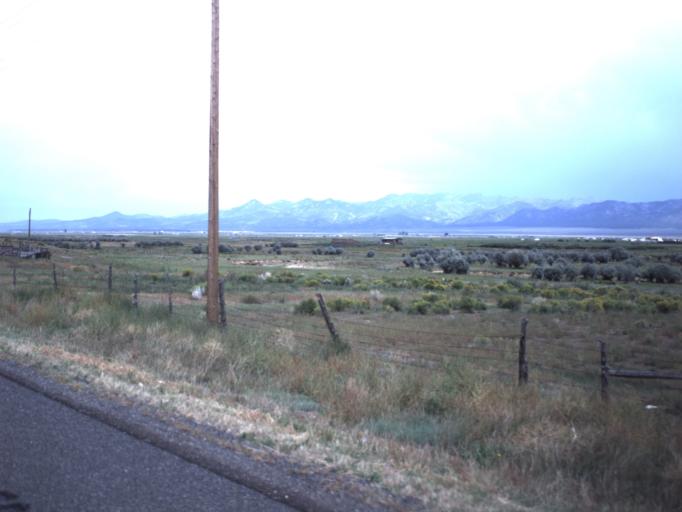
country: US
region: Utah
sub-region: Garfield County
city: Panguitch
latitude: 37.8524
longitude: -112.4390
